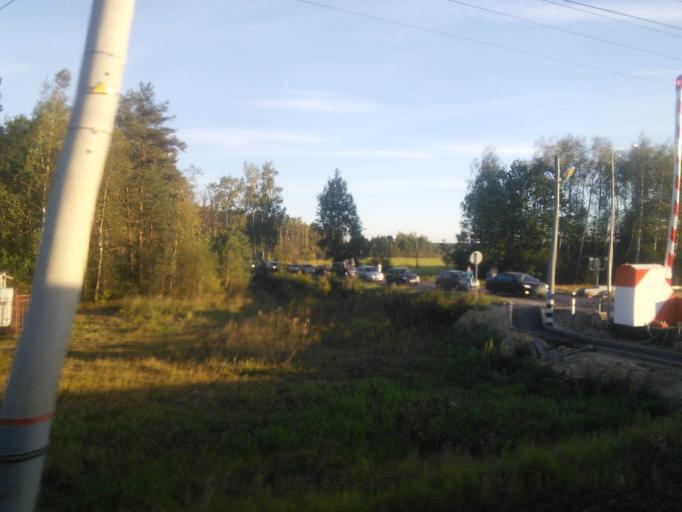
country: RU
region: Moskovskaya
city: Rakhmanovo
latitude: 55.7484
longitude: 38.5380
